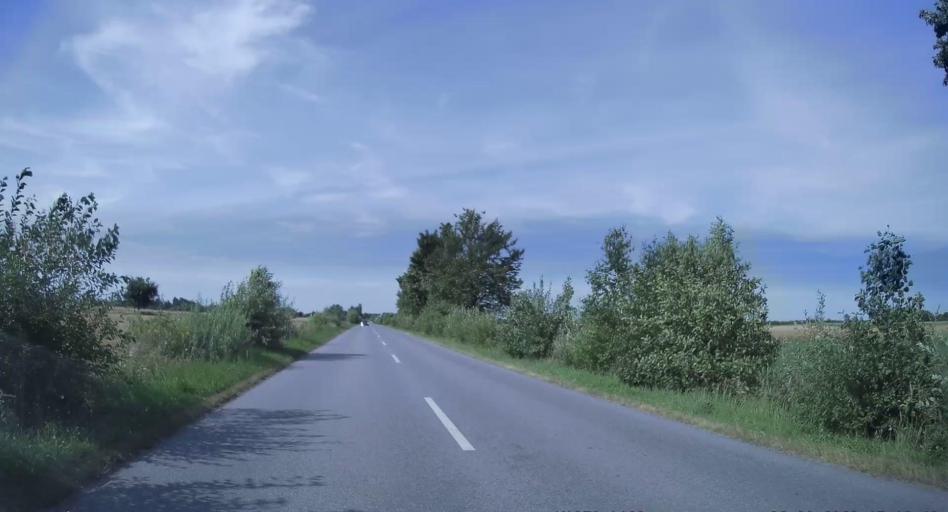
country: PL
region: Lodz Voivodeship
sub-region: Powiat opoczynski
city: Mniszkow
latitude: 51.3813
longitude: 20.0359
